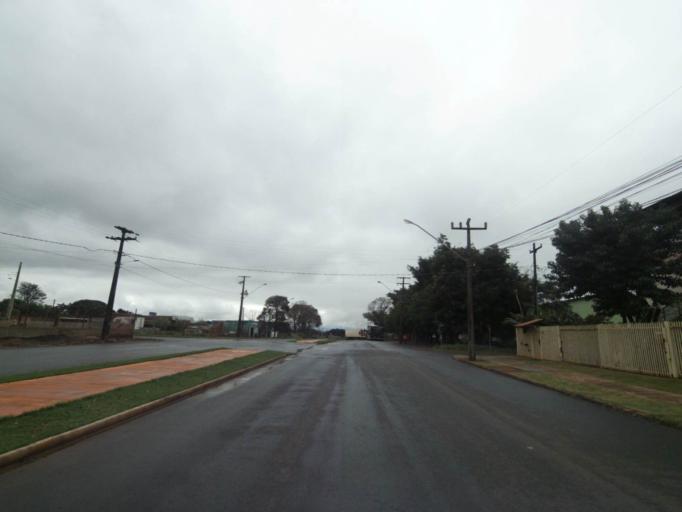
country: BR
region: Parana
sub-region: Foz Do Iguacu
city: Foz do Iguacu
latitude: -25.5136
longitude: -54.5613
